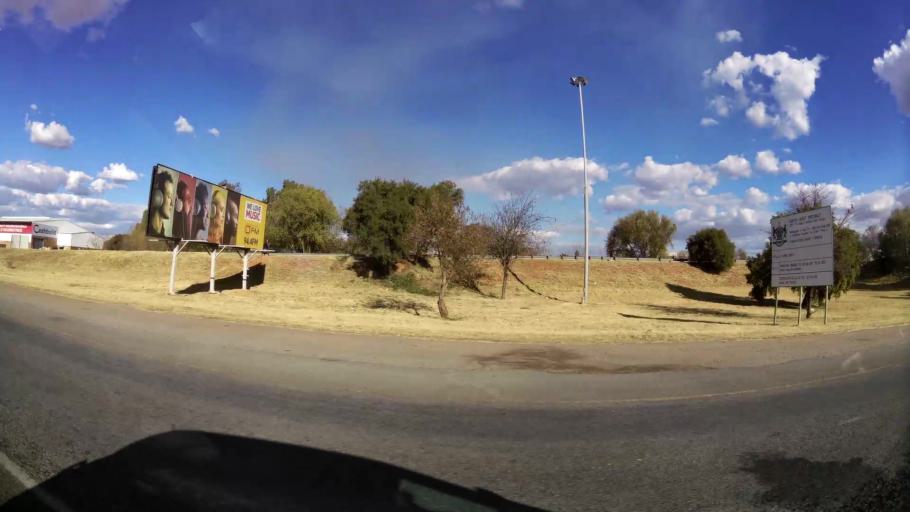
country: ZA
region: North-West
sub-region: Dr Kenneth Kaunda District Municipality
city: Klerksdorp
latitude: -26.8607
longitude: 26.6660
